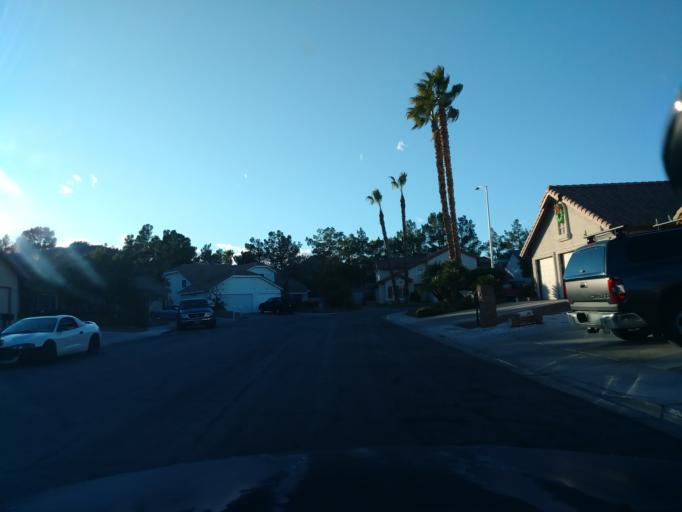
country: US
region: Nevada
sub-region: Clark County
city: Spring Valley
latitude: 36.1464
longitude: -115.2376
